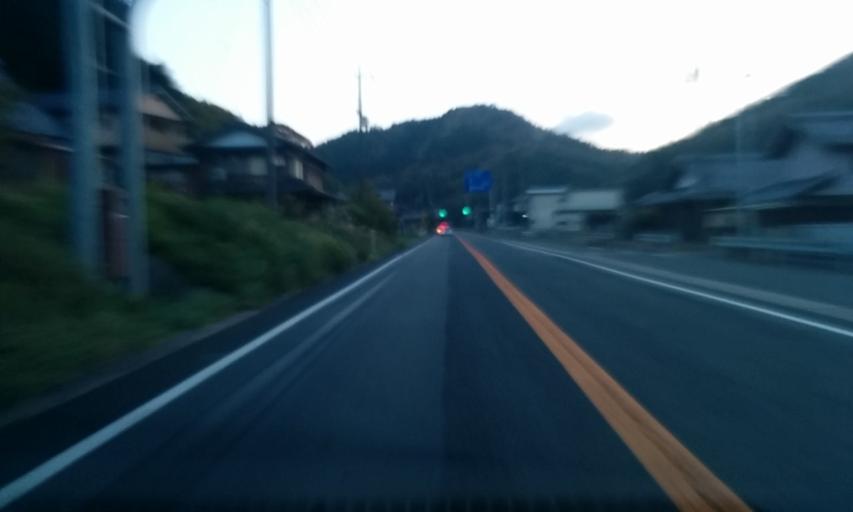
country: JP
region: Kyoto
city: Kameoka
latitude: 35.1414
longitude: 135.4261
